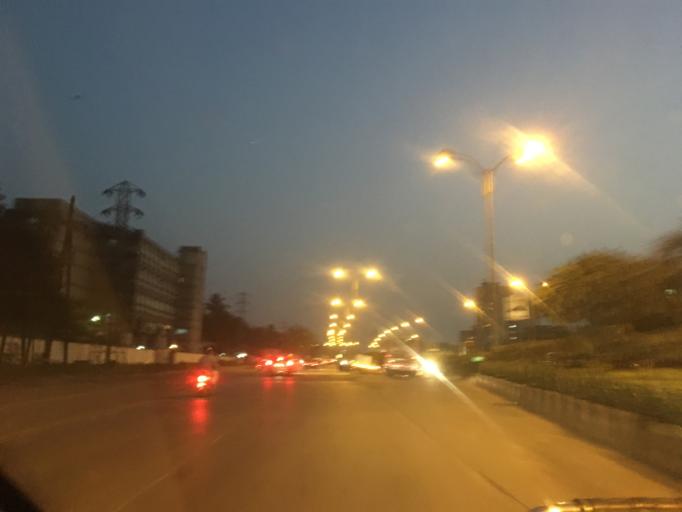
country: IN
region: Maharashtra
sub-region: Thane
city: Airoli
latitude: 19.1500
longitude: 73.0007
